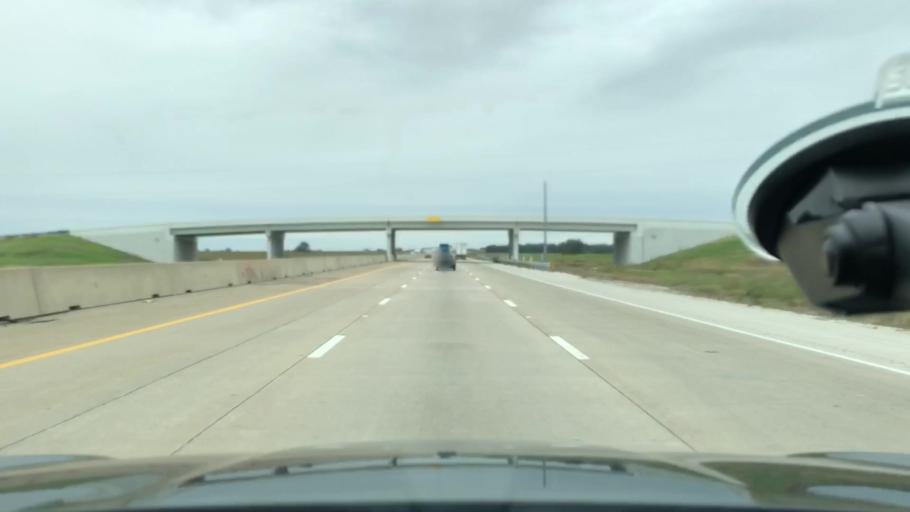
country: US
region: Texas
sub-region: Ellis County
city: Italy
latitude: 32.2451
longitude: -96.8757
